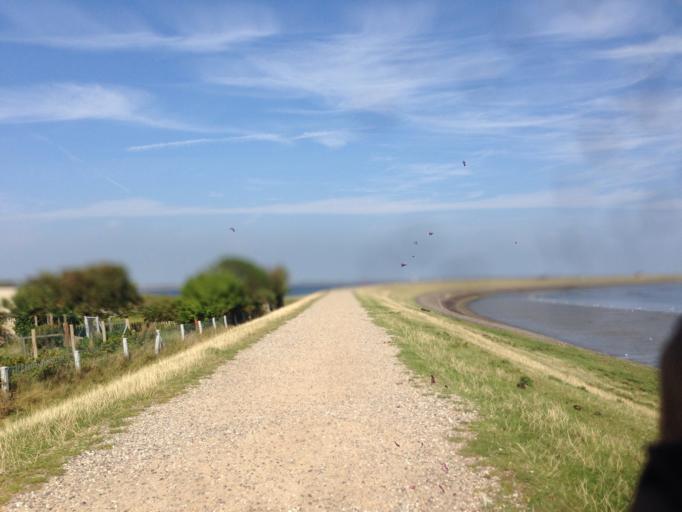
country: DE
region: Schleswig-Holstein
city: Westerland
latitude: 54.8576
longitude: 8.3044
